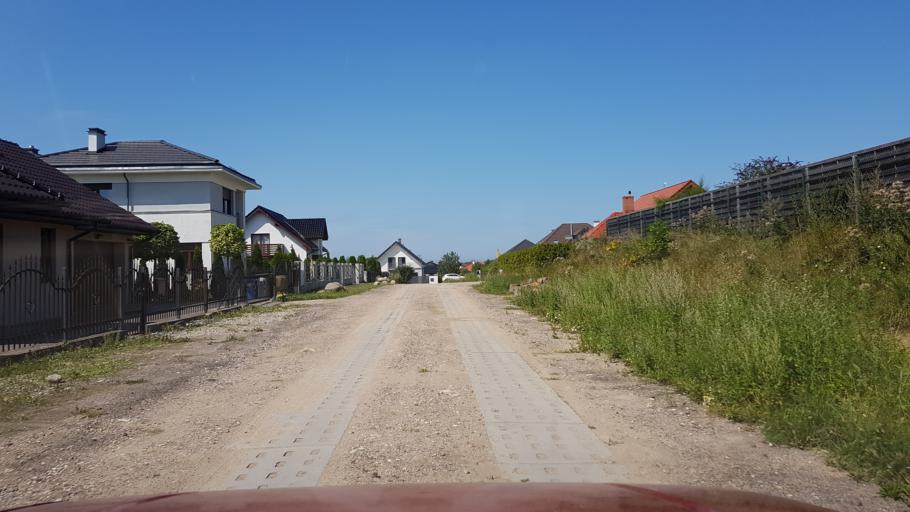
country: PL
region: West Pomeranian Voivodeship
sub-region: Koszalin
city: Koszalin
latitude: 54.2159
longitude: 16.1707
